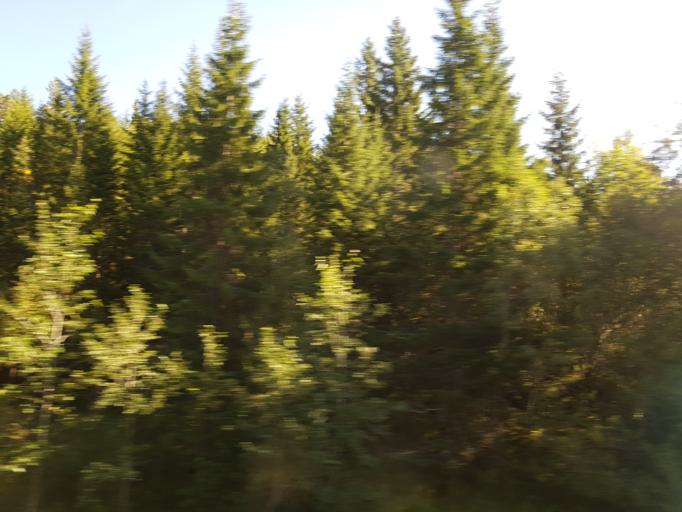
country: NO
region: Sor-Trondelag
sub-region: Afjord
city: A i Afjord
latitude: 63.7386
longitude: 10.2354
